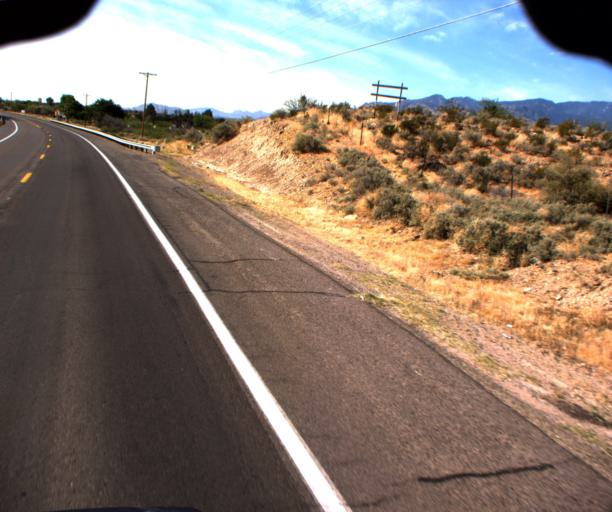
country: US
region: Arizona
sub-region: Graham County
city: Swift Trail Junction
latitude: 32.7356
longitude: -109.7163
